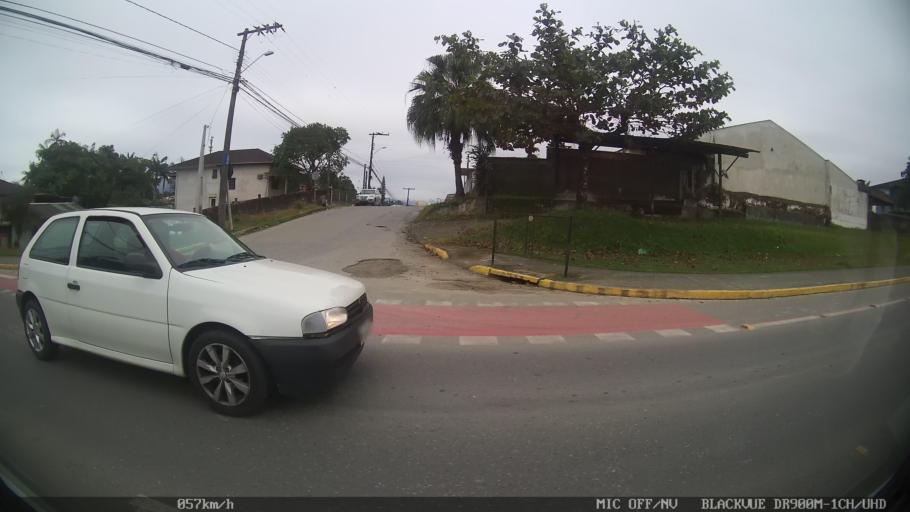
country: BR
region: Santa Catarina
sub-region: Joinville
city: Joinville
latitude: -26.2923
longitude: -48.9030
